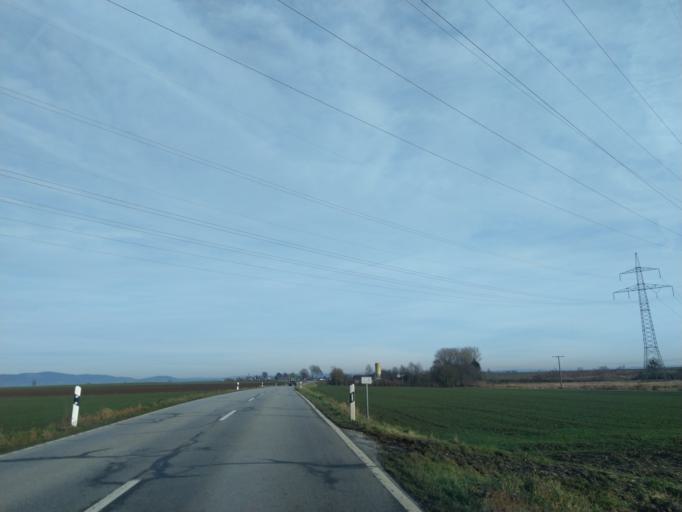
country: DE
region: Bavaria
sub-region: Lower Bavaria
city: Buchhofen
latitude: 48.6991
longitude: 12.9491
